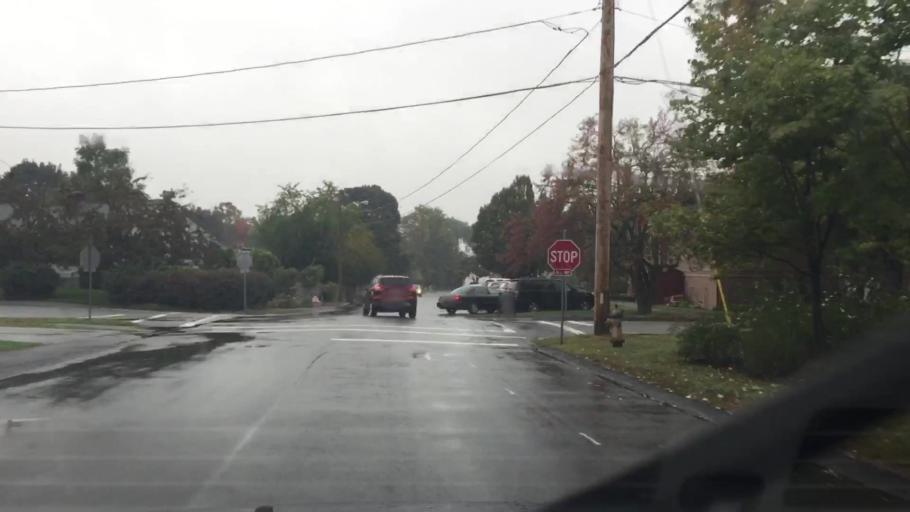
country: US
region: Massachusetts
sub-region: Essex County
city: North Andover
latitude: 42.6949
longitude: -71.1268
